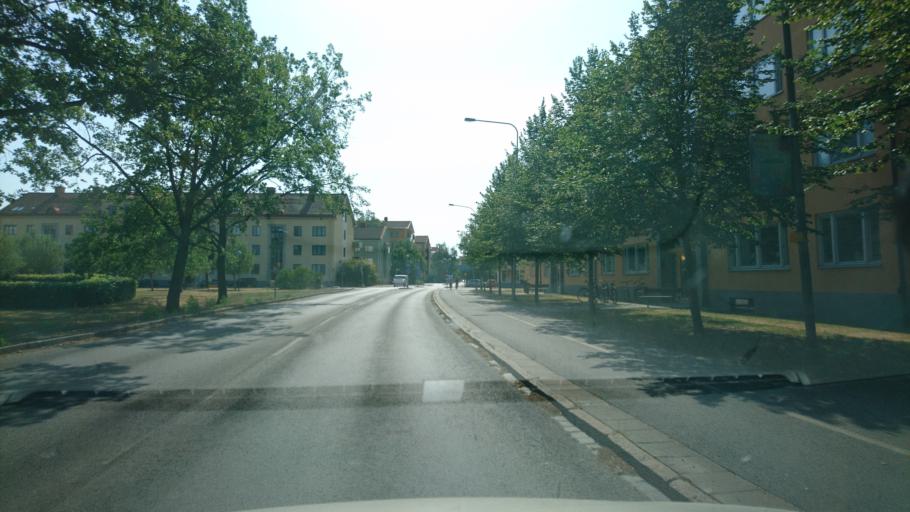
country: SE
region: Uppsala
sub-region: Uppsala Kommun
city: Uppsala
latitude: 59.8622
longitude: 17.6167
